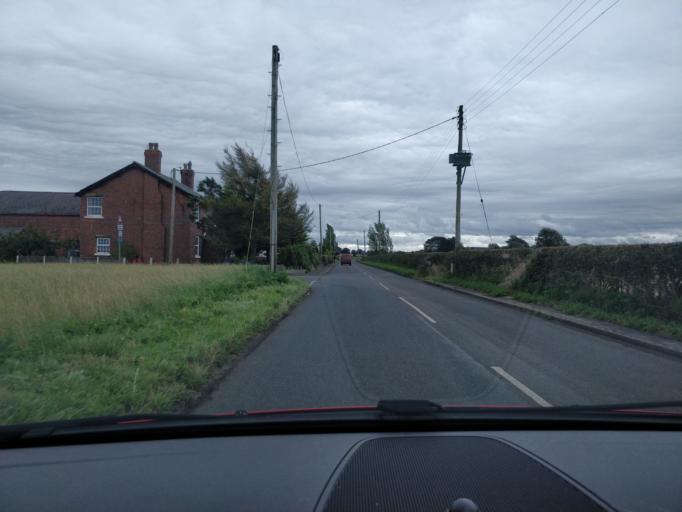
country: GB
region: England
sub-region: Lancashire
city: Ormskirk
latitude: 53.6185
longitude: -2.8500
